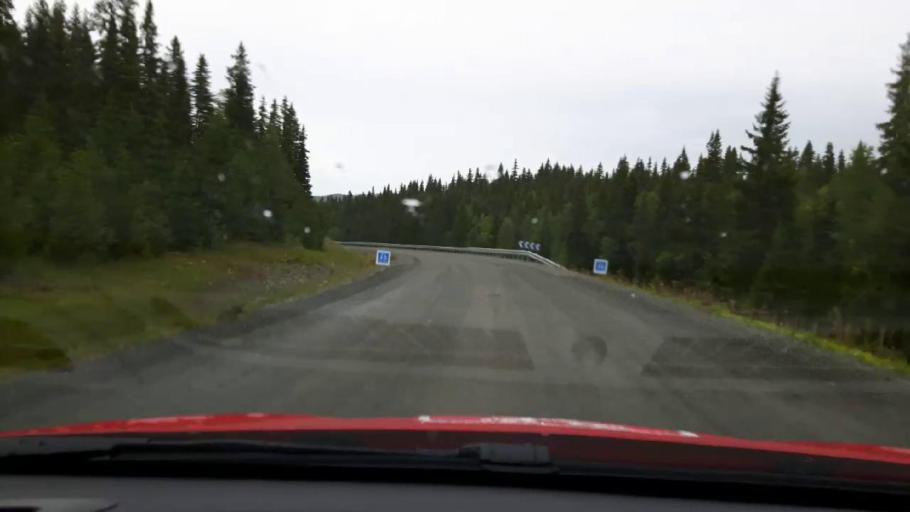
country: SE
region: Jaemtland
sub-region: Are Kommun
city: Are
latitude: 63.4124
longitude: 12.7699
